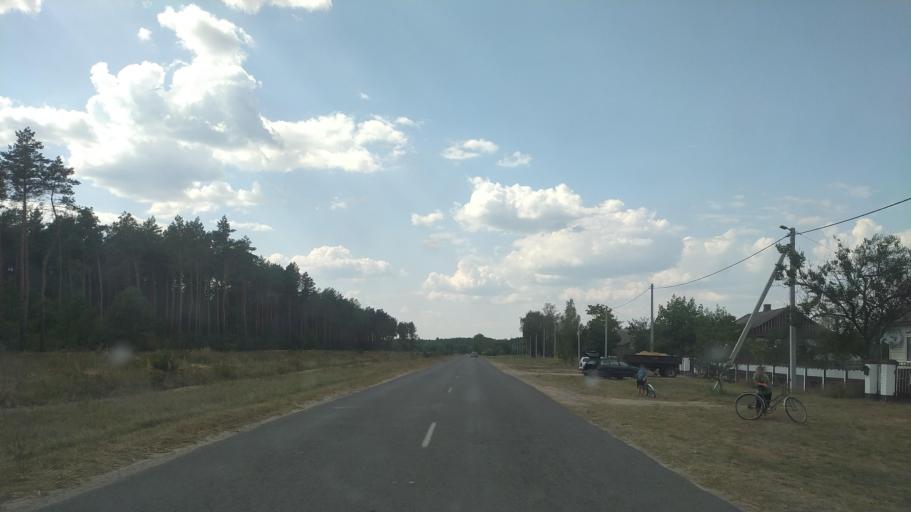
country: BY
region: Brest
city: Drahichyn
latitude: 52.1028
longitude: 25.1384
